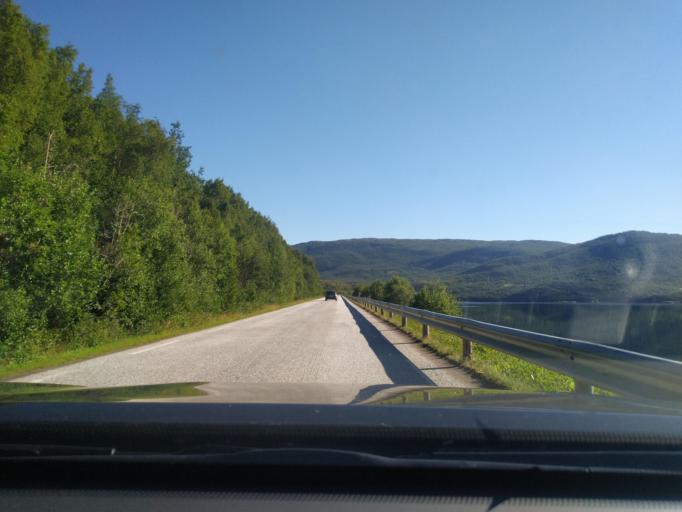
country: NO
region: Troms
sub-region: Dyroy
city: Brostadbotn
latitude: 68.9319
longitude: 17.6776
